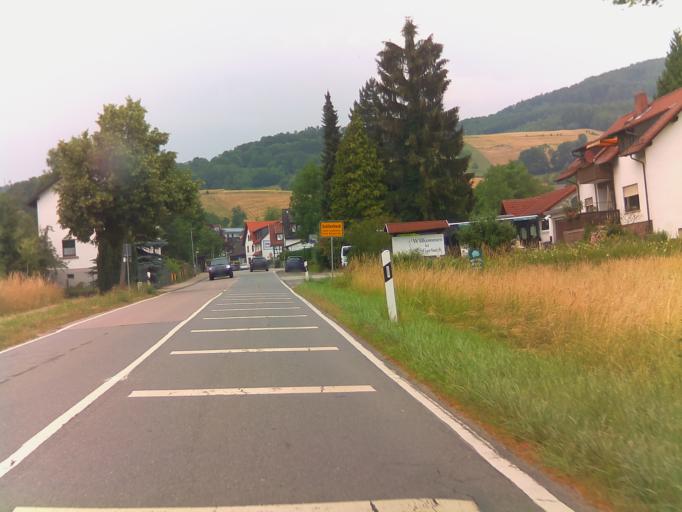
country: DE
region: Hesse
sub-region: Regierungsbezirk Darmstadt
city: Lindenfels
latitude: 49.6801
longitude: 8.7661
